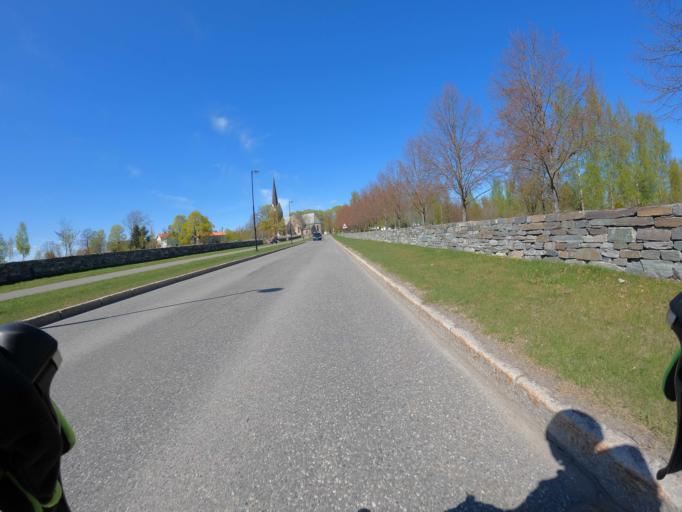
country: NO
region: Akershus
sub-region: Skedsmo
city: Lillestrom
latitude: 59.9921
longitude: 11.0473
